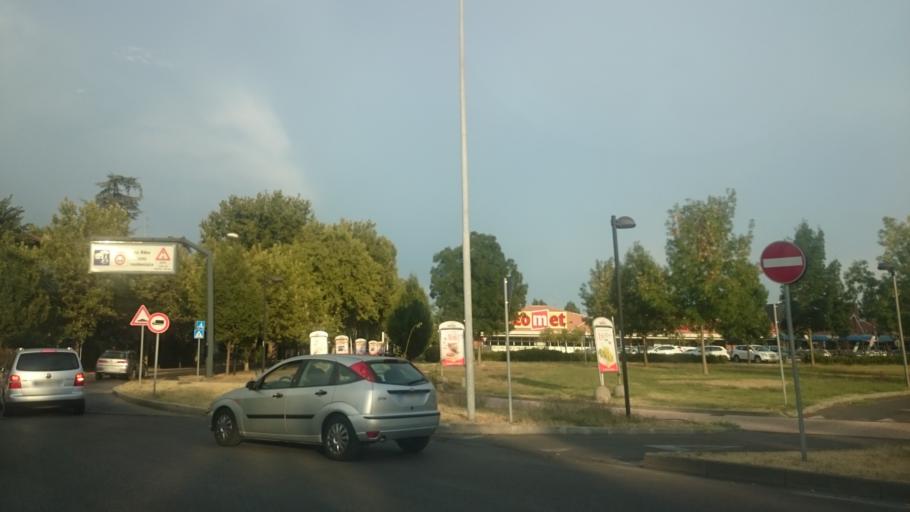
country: IT
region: Emilia-Romagna
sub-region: Provincia di Reggio Emilia
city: Reggio nell'Emilia
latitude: 44.7074
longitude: 10.6392
